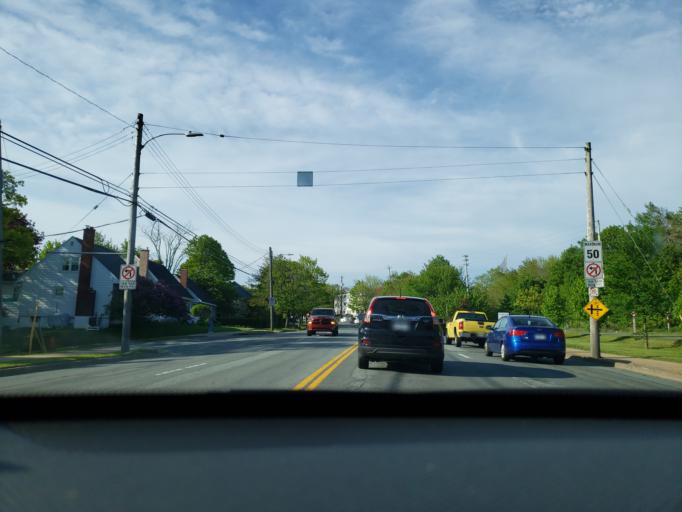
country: CA
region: Nova Scotia
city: Dartmouth
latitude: 44.6512
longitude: -63.6306
